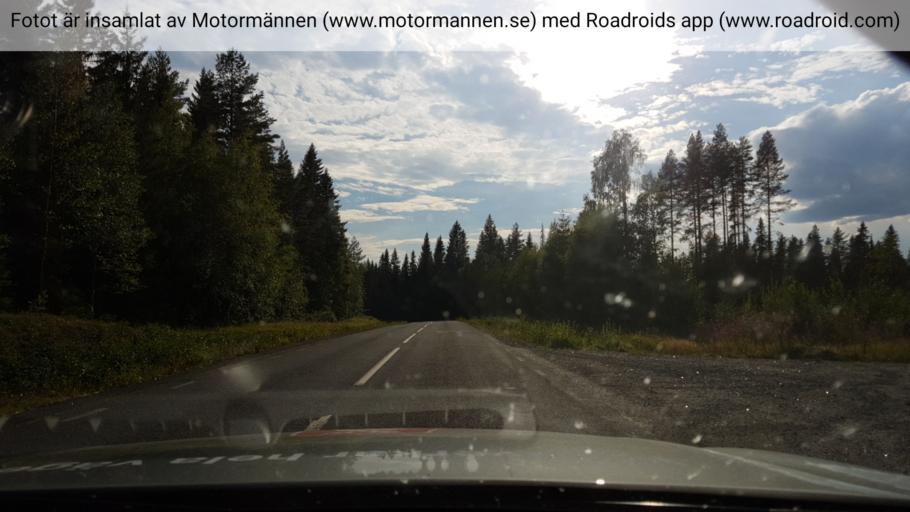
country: SE
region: Vaesternorrland
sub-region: Solleftea Kommun
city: As
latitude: 63.5682
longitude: 16.2406
